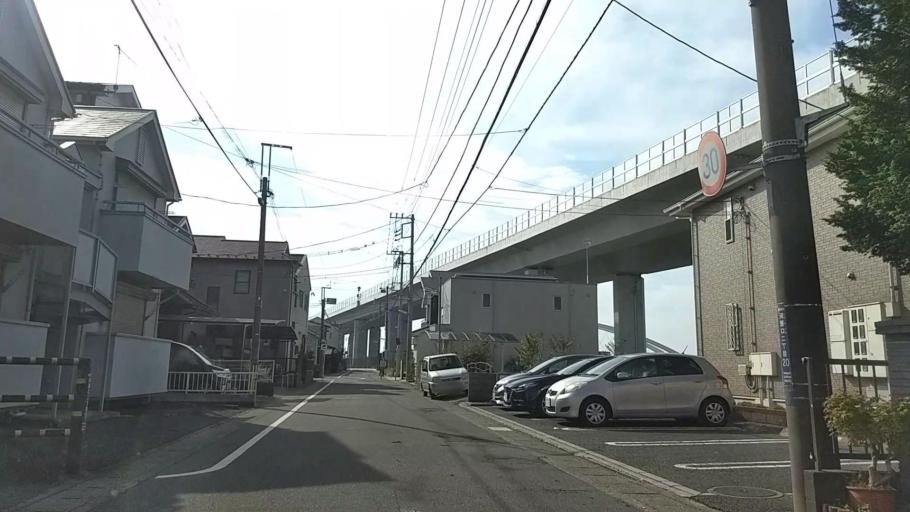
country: JP
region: Kanagawa
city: Atsugi
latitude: 35.4483
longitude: 139.3743
